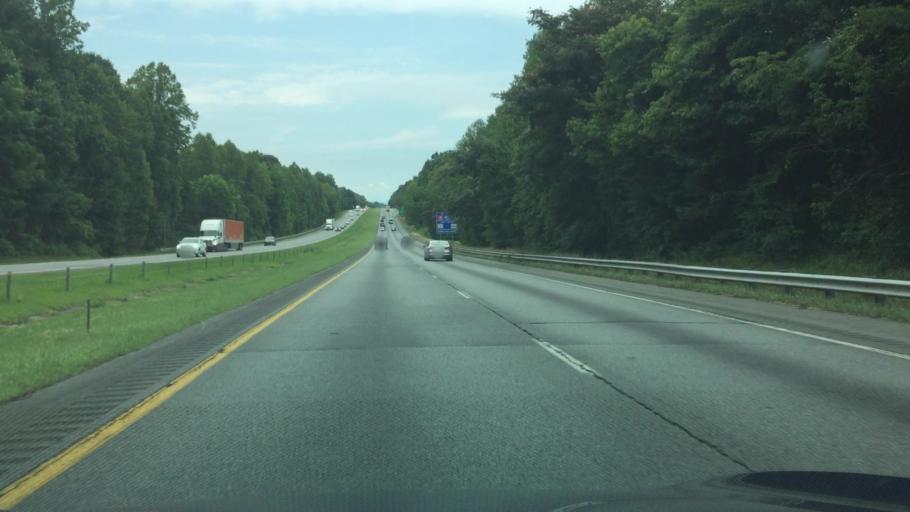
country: US
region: North Carolina
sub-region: Yadkin County
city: Jonesville
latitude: 36.2304
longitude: -80.8148
